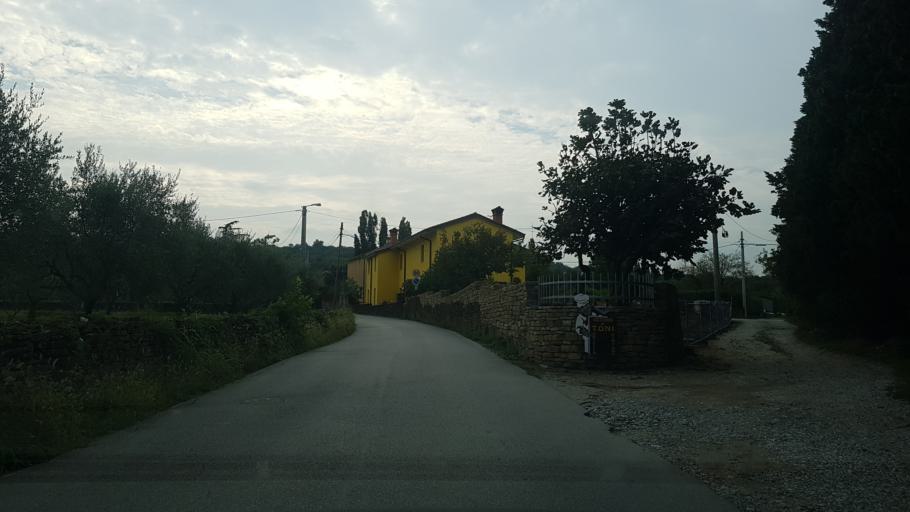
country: SI
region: Koper-Capodistria
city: Spodnje Skofije
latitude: 45.5833
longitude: 13.8016
